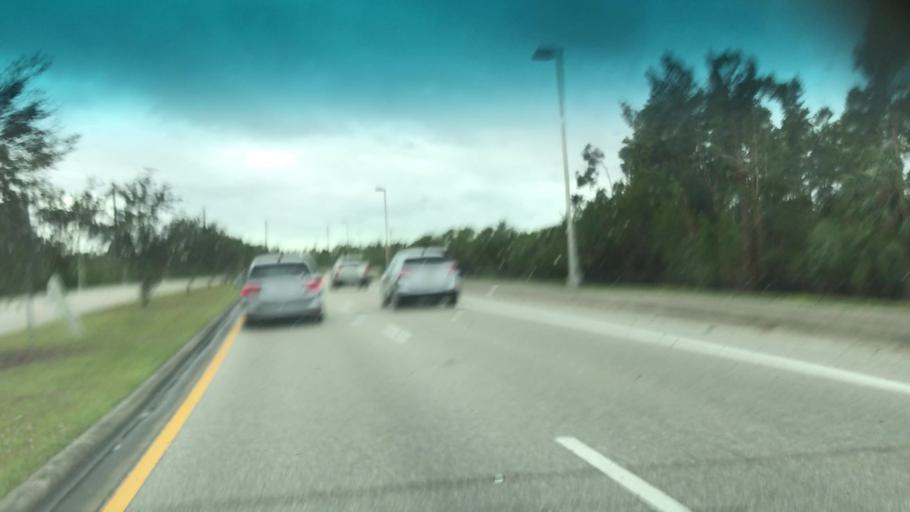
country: US
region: Florida
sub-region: Lee County
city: Harlem Heights
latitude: 26.5195
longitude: -81.9206
